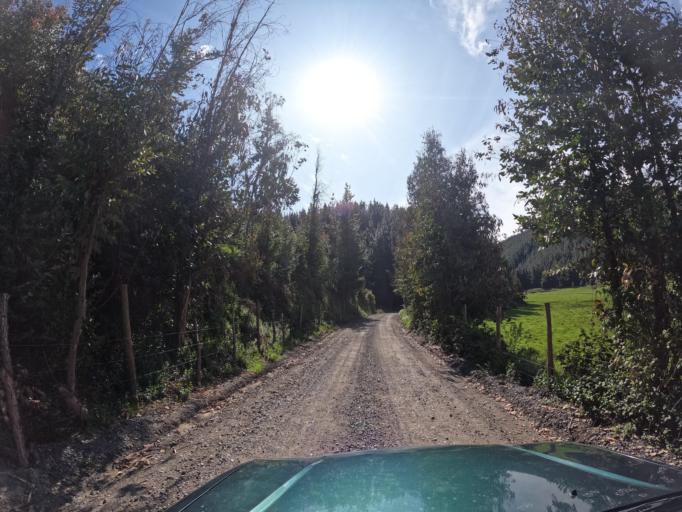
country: CL
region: Biobio
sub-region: Provincia de Concepcion
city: Chiguayante
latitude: -37.0649
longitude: -72.8978
